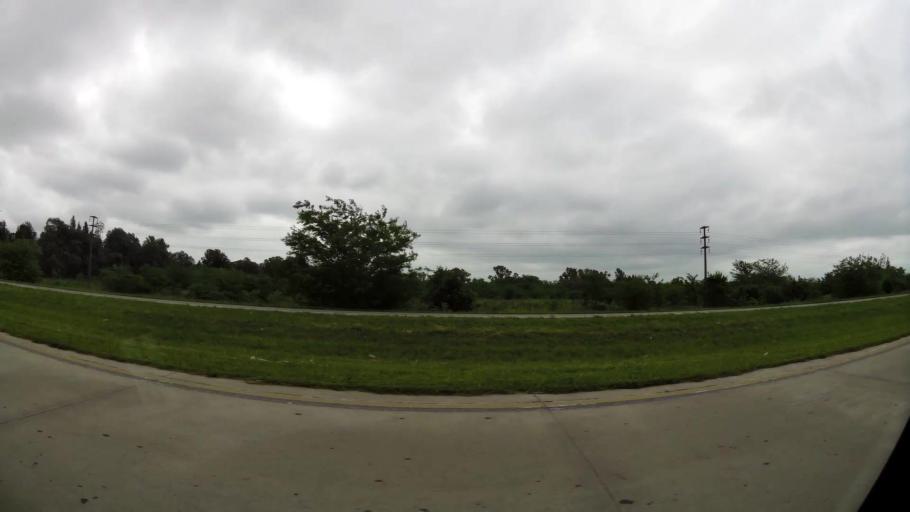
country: AR
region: Buenos Aires
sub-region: Partido de San Vicente
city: San Vicente
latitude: -35.0499
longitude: -58.4292
